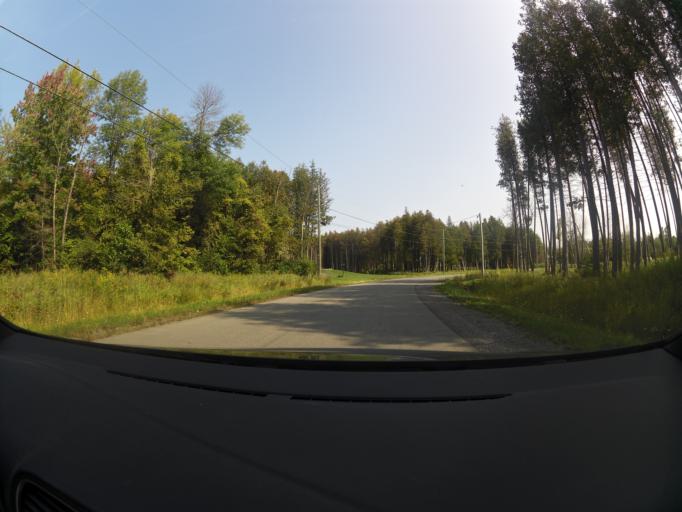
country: CA
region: Ontario
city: Carleton Place
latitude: 45.3260
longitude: -76.1546
